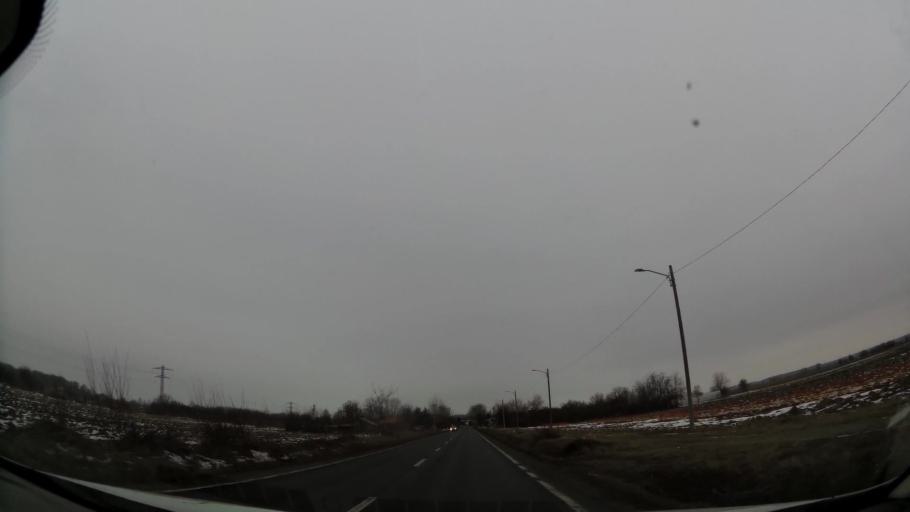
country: RO
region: Dambovita
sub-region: Comuna Contesti
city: Contesti
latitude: 44.6779
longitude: 25.6461
